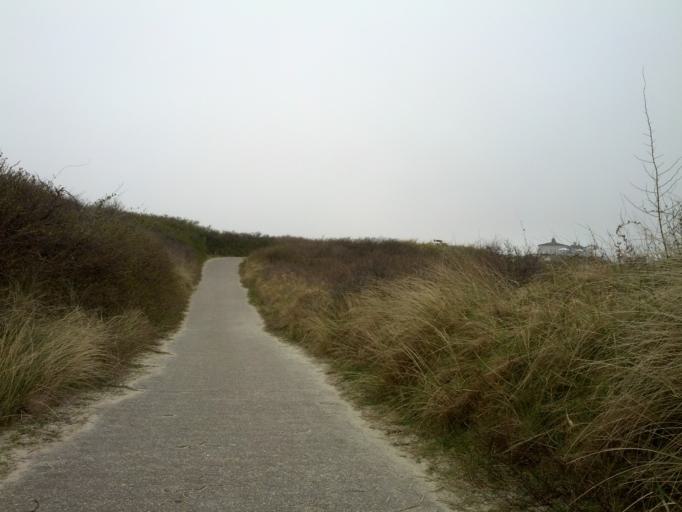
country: DE
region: Lower Saxony
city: Langeoog
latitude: 53.7489
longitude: 7.4742
